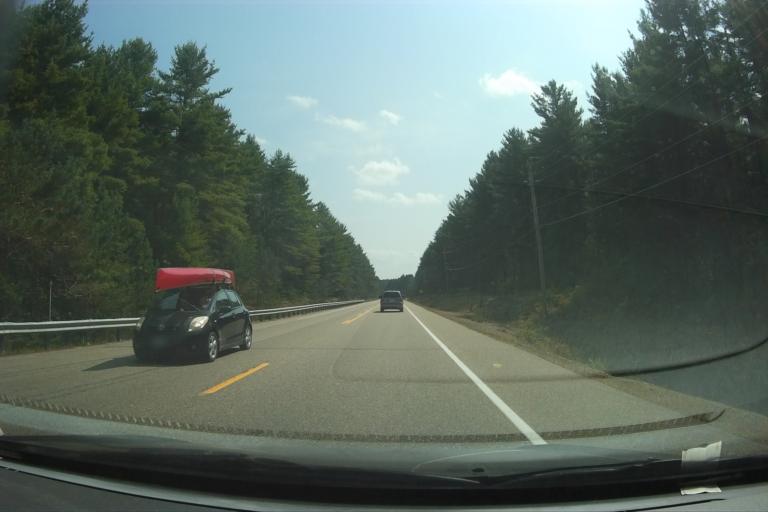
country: CA
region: Ontario
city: Bancroft
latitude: 45.5743
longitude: -78.4462
